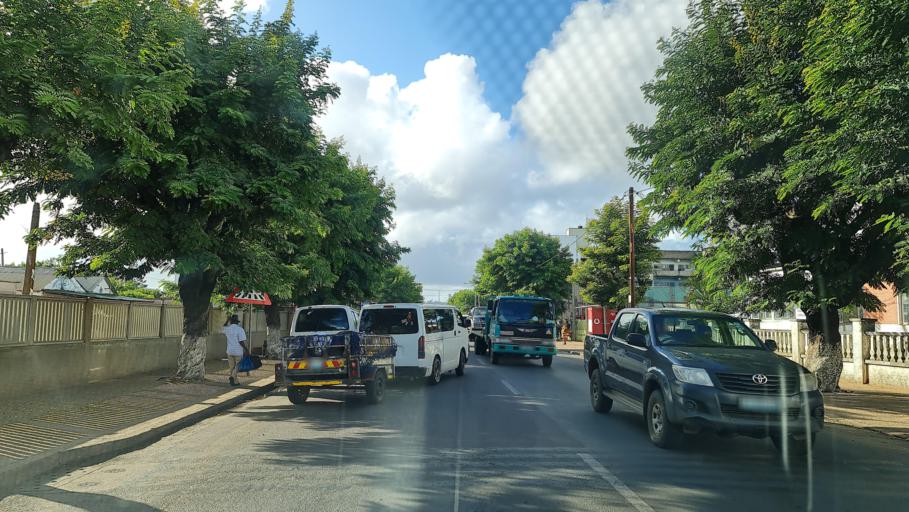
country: MZ
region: Gaza
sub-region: Xai-Xai District
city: Xai-Xai
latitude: -25.0401
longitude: 33.6400
